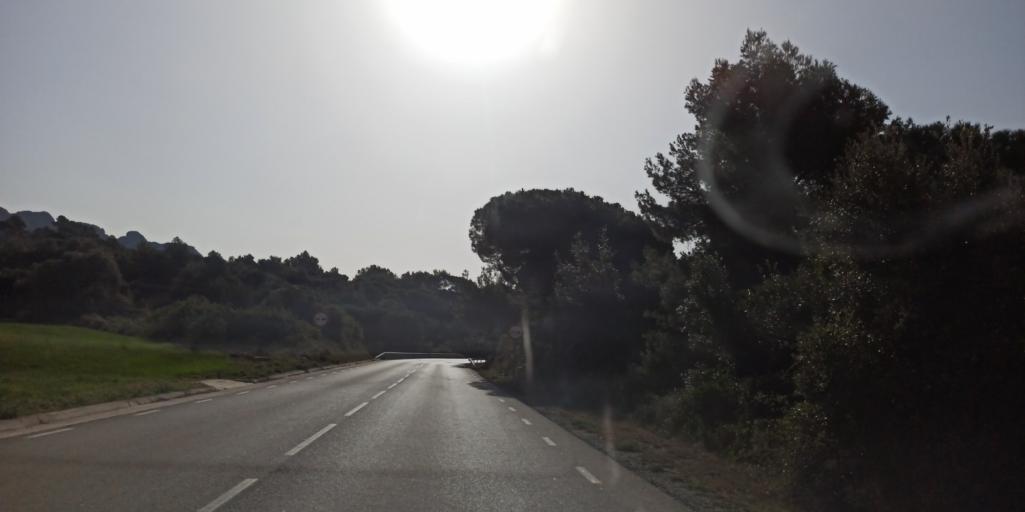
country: ES
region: Catalonia
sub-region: Provincia de Barcelona
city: Castelloli
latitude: 41.6010
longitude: 1.7618
